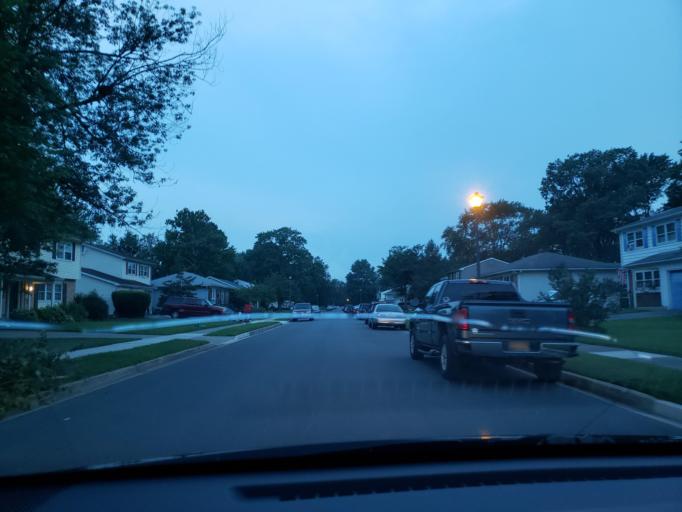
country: US
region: Delaware
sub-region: Kent County
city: Rodney Village
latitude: 39.1352
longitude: -75.5352
